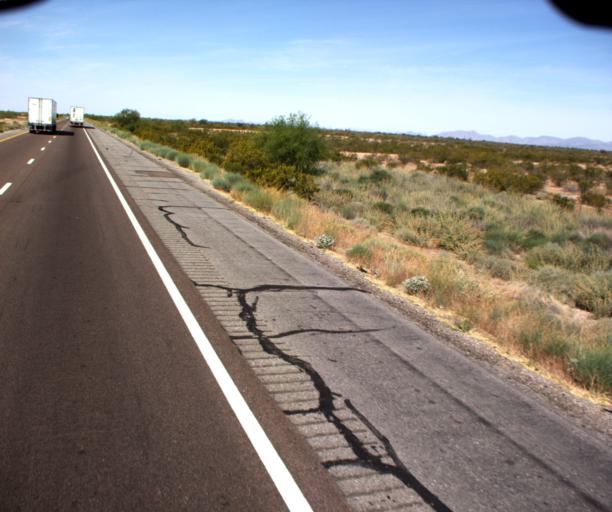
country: US
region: Arizona
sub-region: La Paz County
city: Salome
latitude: 33.5476
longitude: -113.2103
